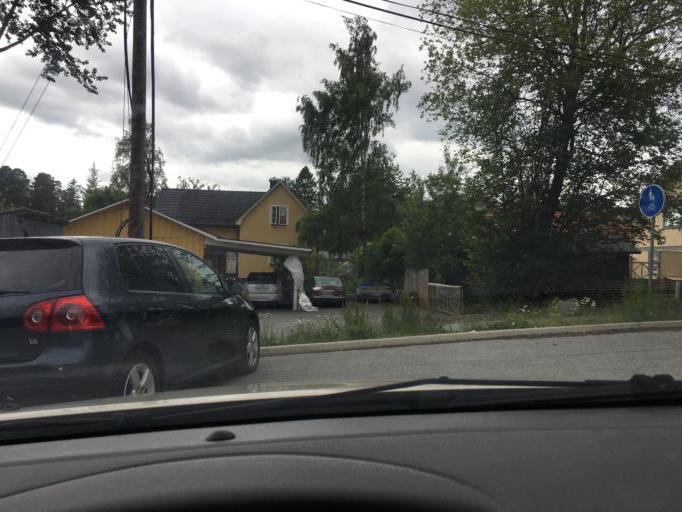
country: SE
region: Stockholm
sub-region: Nacka Kommun
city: Fisksatra
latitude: 59.3064
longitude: 18.2568
